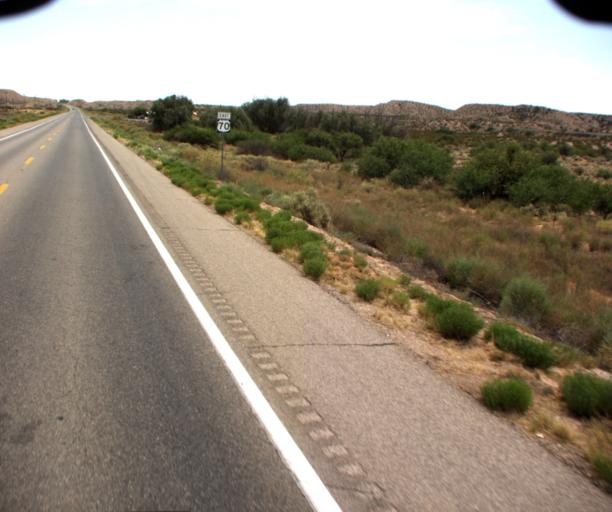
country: US
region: Arizona
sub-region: Graham County
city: Bylas
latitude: 33.0853
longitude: -110.0536
